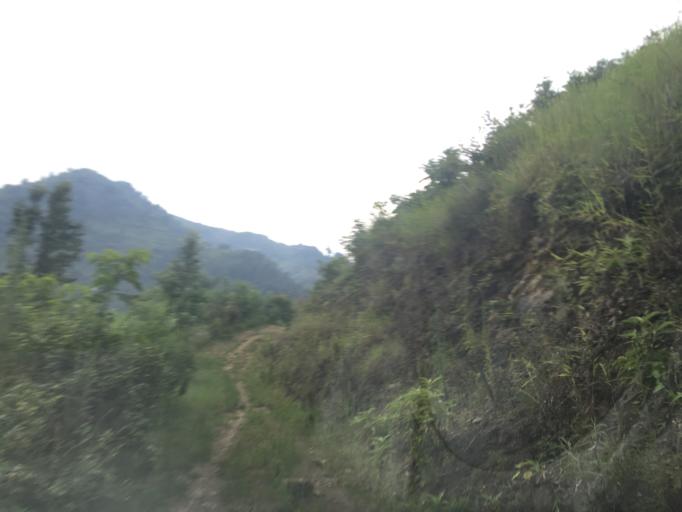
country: CN
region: Guangxi Zhuangzu Zizhiqu
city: Xinzhou
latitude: 25.1677
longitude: 105.6998
